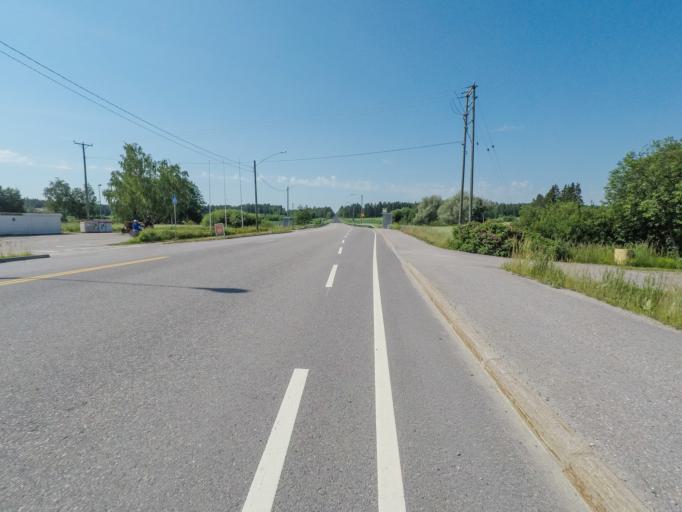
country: FI
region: Uusimaa
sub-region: Helsinki
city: Nickby
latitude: 60.3116
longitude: 25.3884
